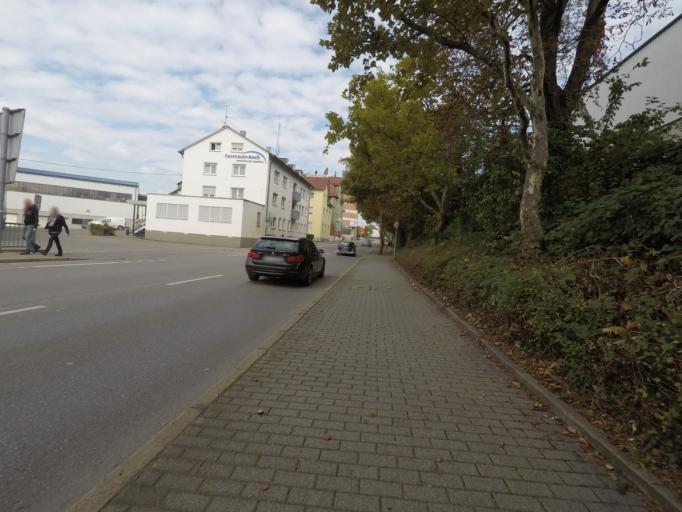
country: DE
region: Baden-Wuerttemberg
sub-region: Tuebingen Region
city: Reutlingen
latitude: 48.5019
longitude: 9.2116
